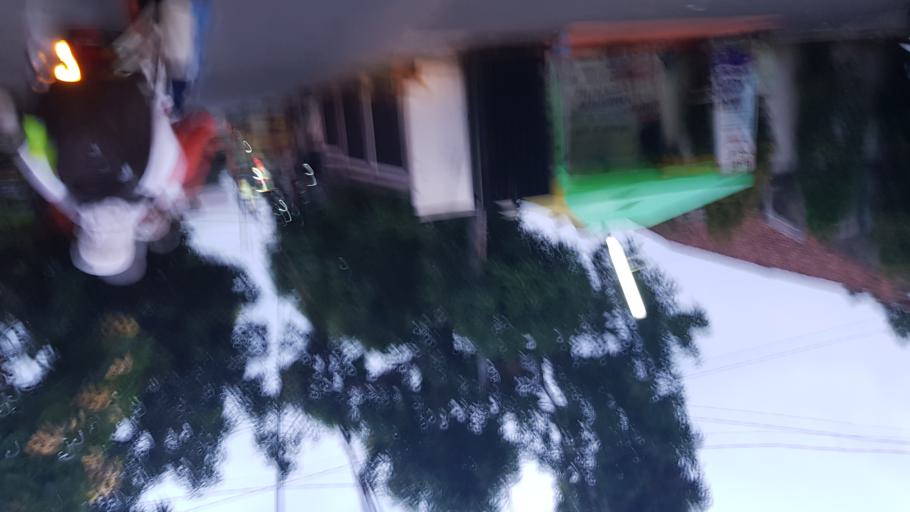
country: ID
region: West Java
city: Depok
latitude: -6.3682
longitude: 106.8050
